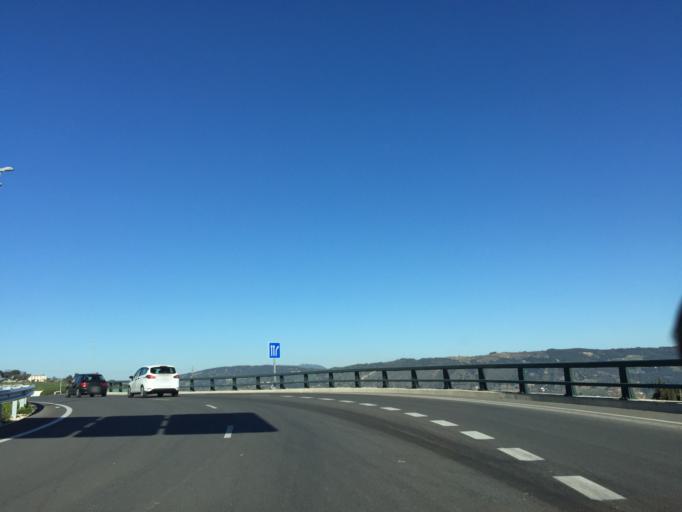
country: ES
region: Andalusia
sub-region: Provincia de Malaga
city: Ronda
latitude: 36.7547
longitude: -5.1489
